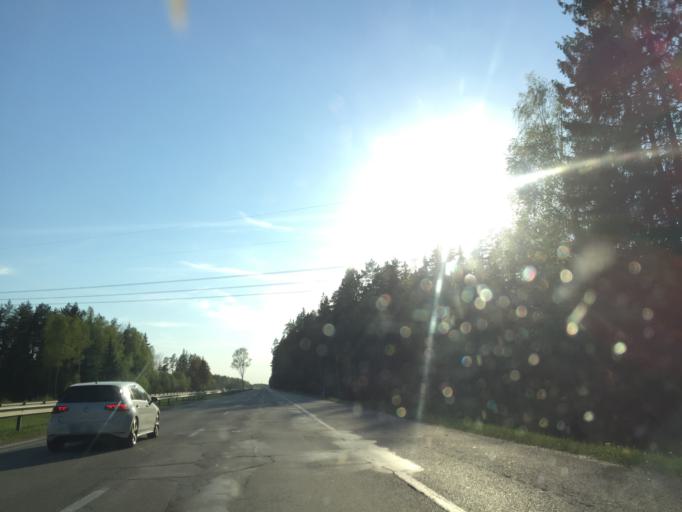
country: LV
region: Krimulda
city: Ragana
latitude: 57.1329
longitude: 24.7541
